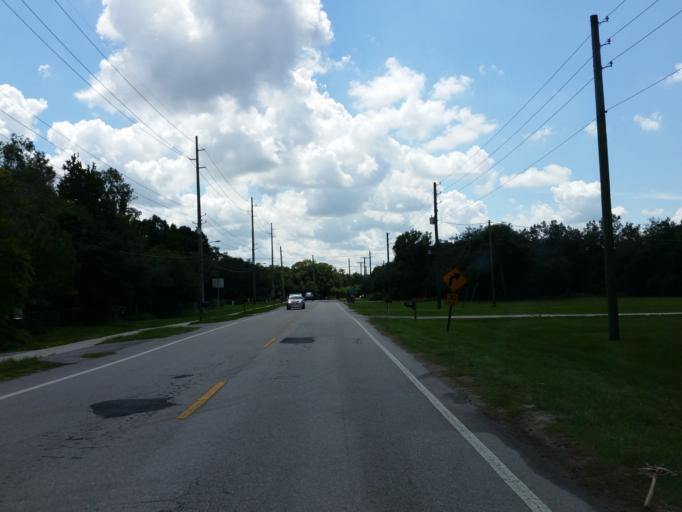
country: US
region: Florida
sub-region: Hillsborough County
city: Riverview
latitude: 27.8333
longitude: -82.3020
